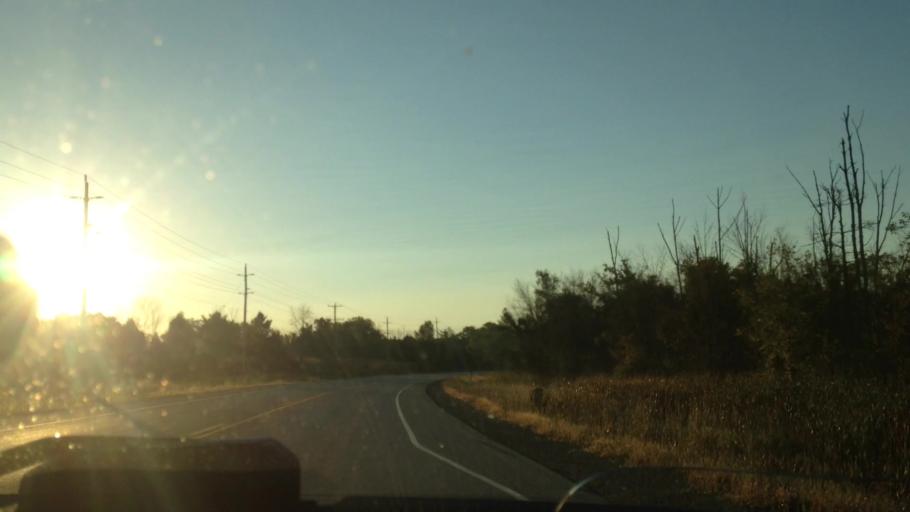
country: US
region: Wisconsin
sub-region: Washington County
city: Newburg
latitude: 43.4066
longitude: -87.9945
